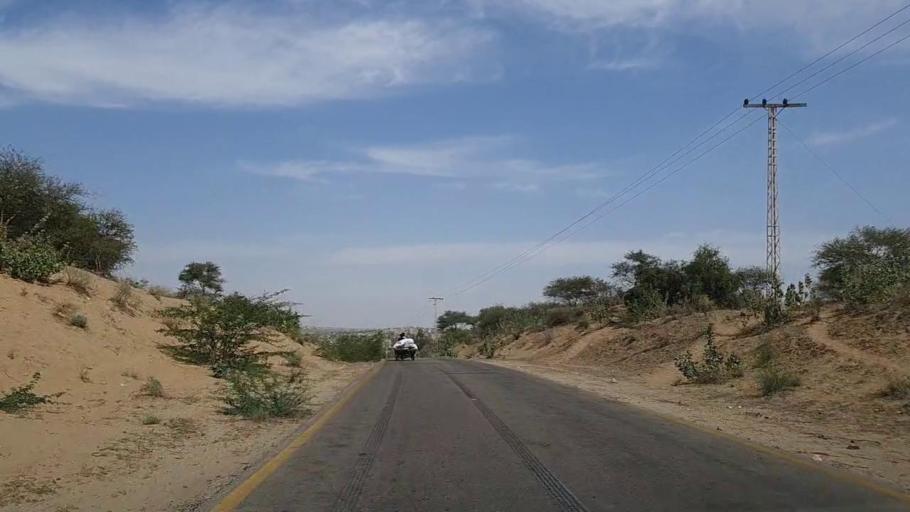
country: PK
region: Sindh
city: Mithi
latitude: 24.7810
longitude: 69.8102
